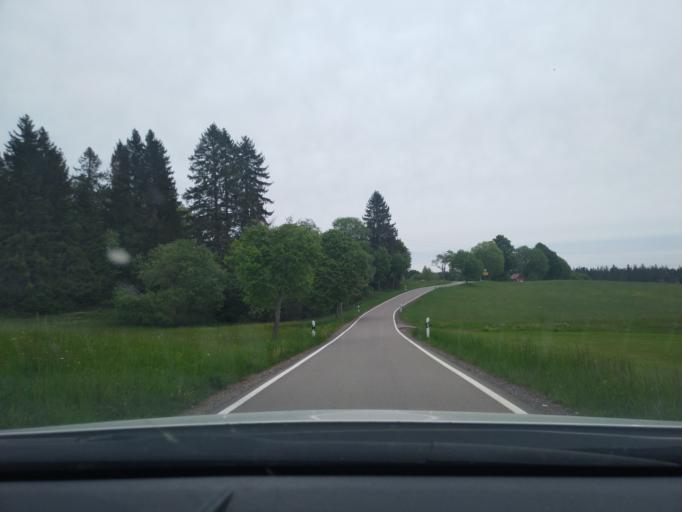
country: DE
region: Baden-Wuerttemberg
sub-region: Freiburg Region
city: Schluchsee
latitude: 47.8055
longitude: 8.2323
